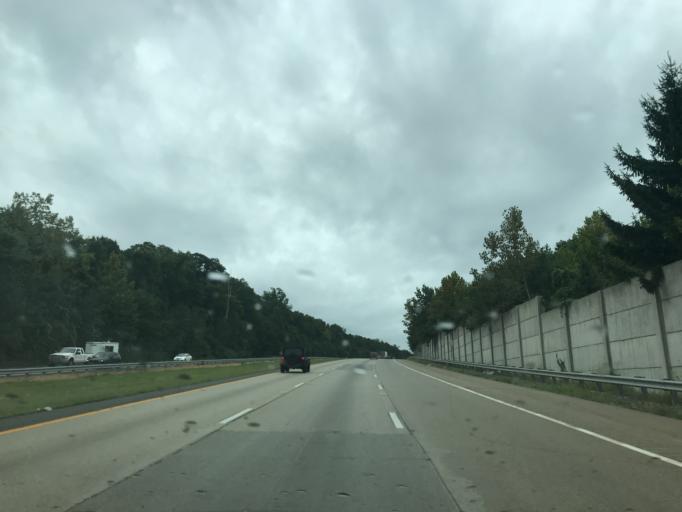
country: US
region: New Jersey
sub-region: Bergen County
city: Mahwah
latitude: 41.0868
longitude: -74.1685
